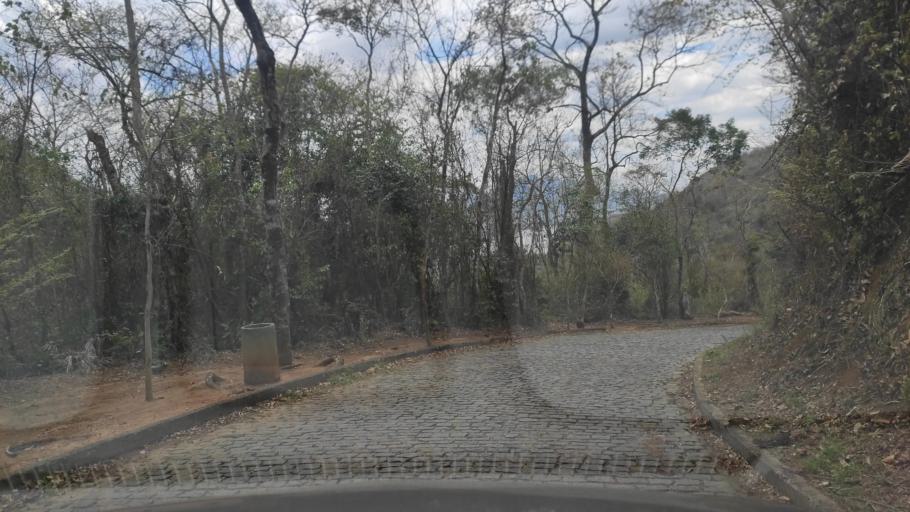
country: BR
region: Espirito Santo
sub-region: Vitoria
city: Vitoria
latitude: -20.2981
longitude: -40.3380
